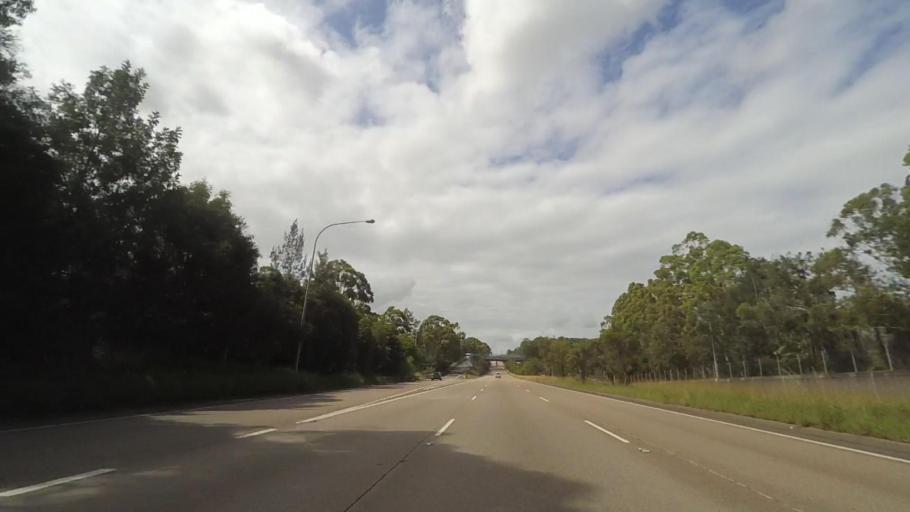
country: AU
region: New South Wales
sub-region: Newcastle
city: North Lambton
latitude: -32.8995
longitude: 151.6942
